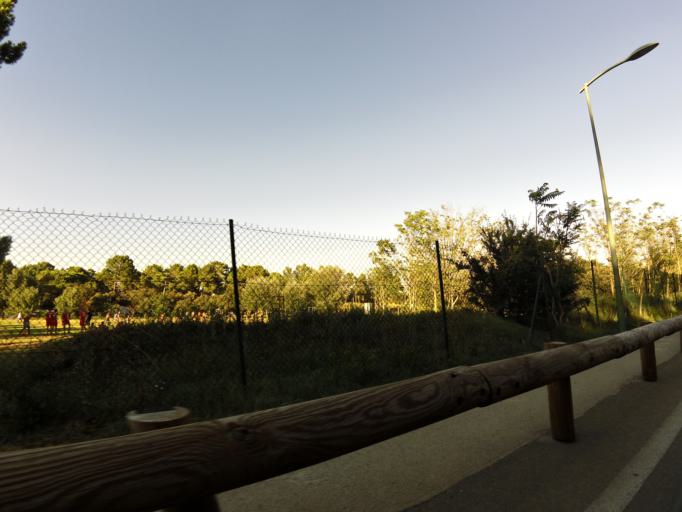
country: FR
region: Languedoc-Roussillon
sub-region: Departement du Gard
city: Castillon-du-Gard
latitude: 43.9474
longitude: 4.5466
